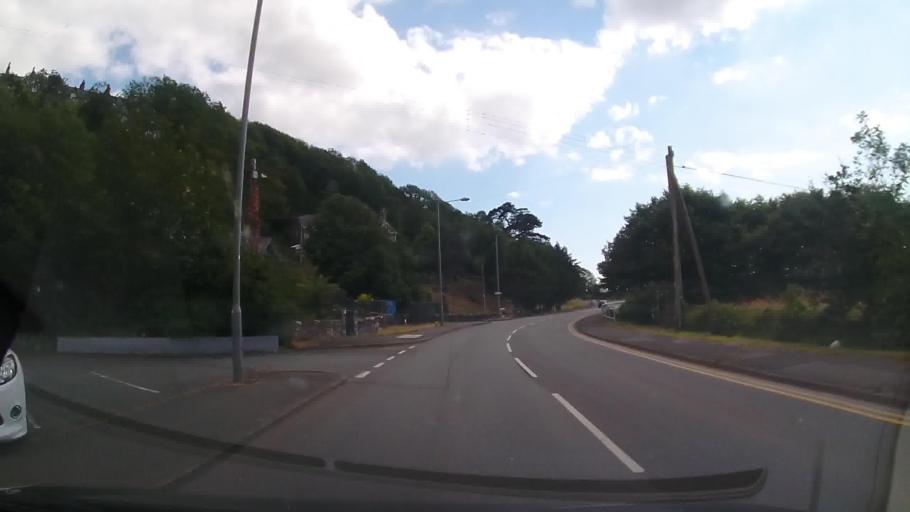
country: GB
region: Wales
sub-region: Gwynedd
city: Llanfair
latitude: 52.8589
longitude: -4.1112
